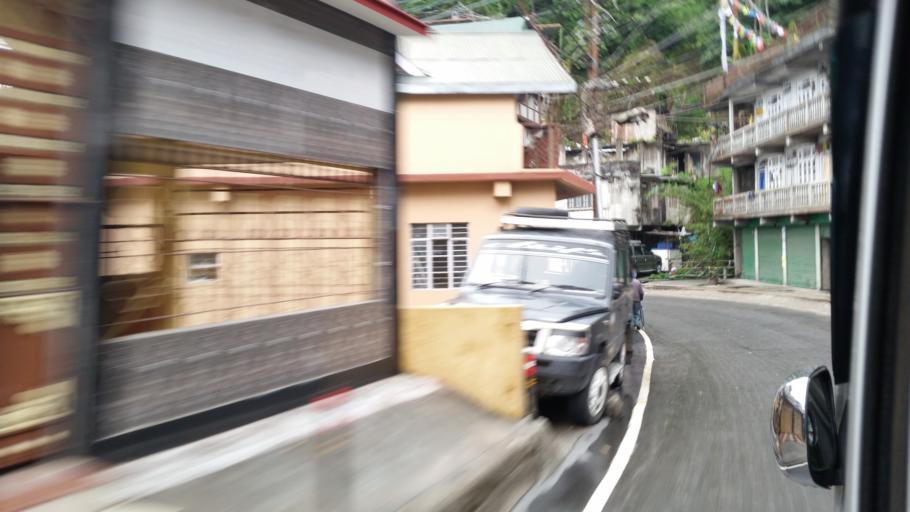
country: IN
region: West Bengal
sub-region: Darjiling
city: Darjiling
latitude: 27.0294
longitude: 88.2574
